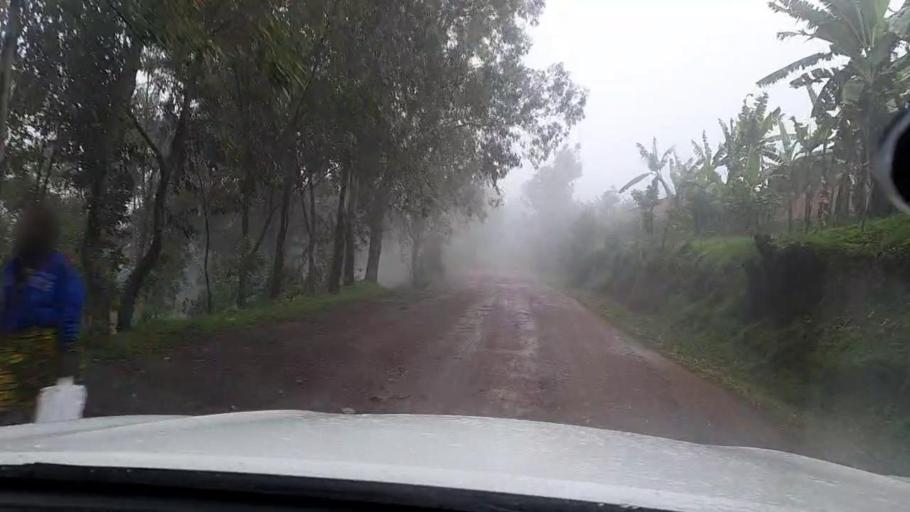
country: RW
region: Kigali
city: Kigali
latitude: -1.7729
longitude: 29.9990
